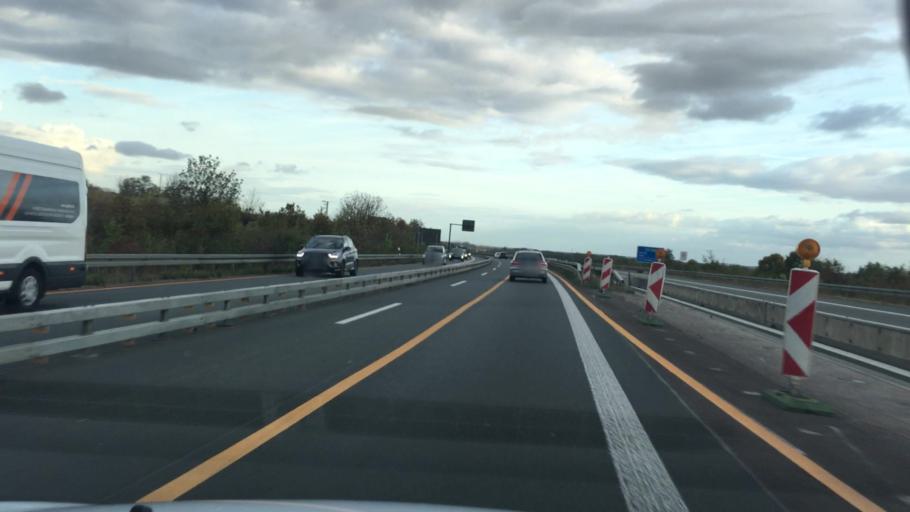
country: DE
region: Saxony-Anhalt
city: Plotzkau
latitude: 51.7284
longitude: 11.6750
